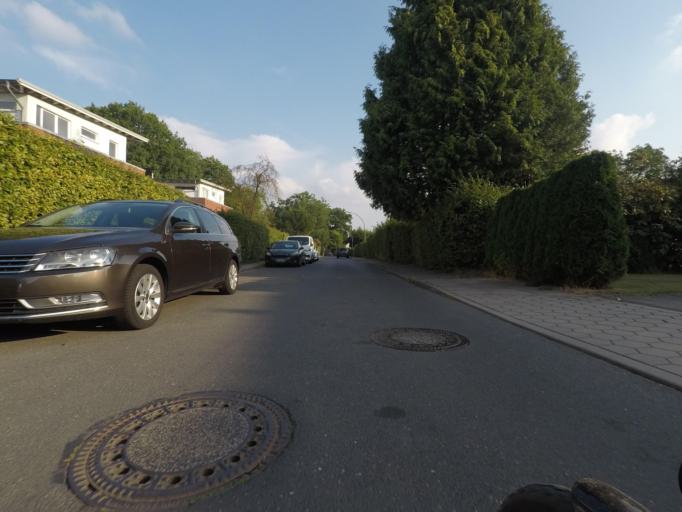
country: DE
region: Hamburg
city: Sasel
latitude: 53.6458
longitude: 10.1101
